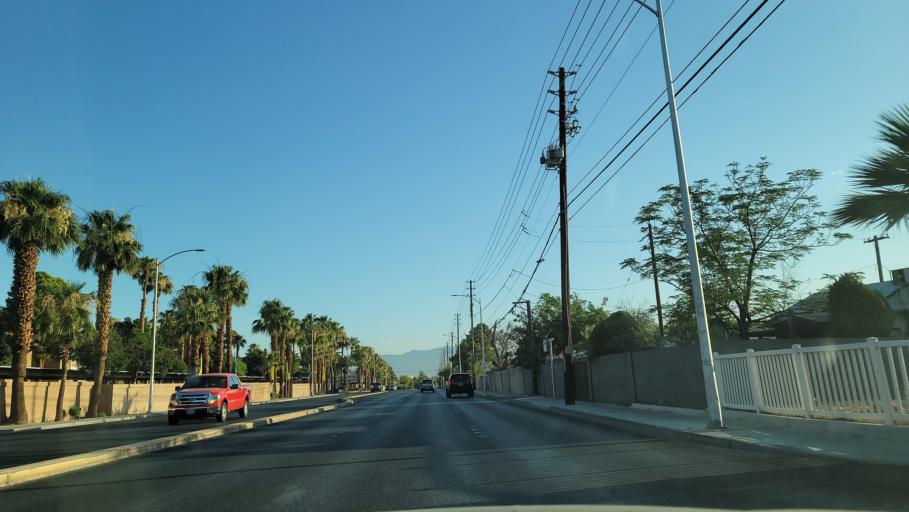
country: US
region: Nevada
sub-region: Clark County
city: Las Vegas
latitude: 36.1520
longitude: -115.1907
